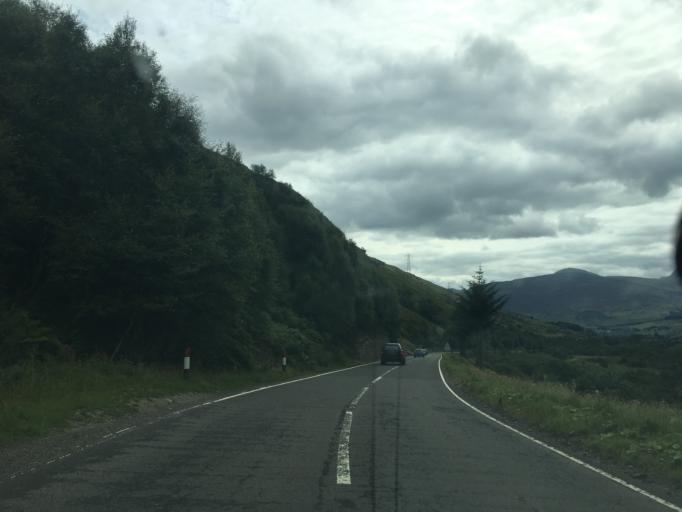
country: GB
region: Scotland
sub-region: Stirling
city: Callander
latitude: 56.4102
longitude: -4.3129
